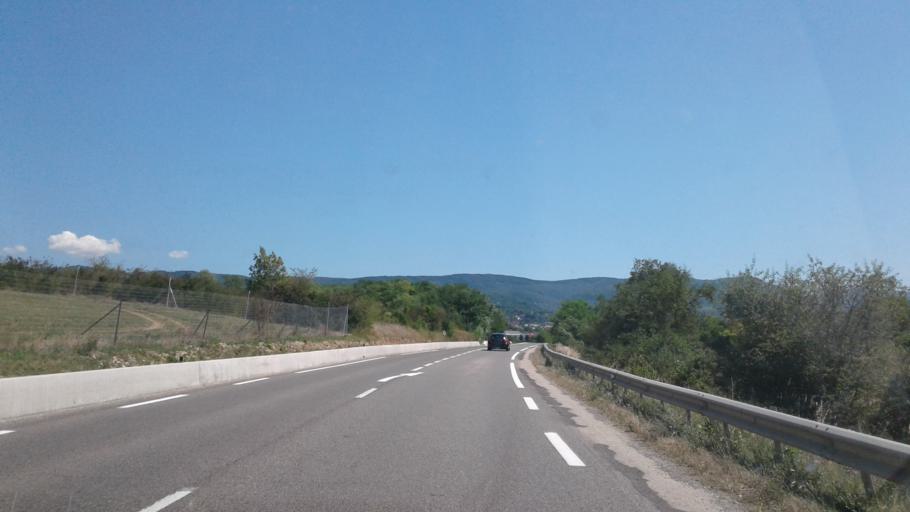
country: FR
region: Rhone-Alpes
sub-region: Departement de l'Ain
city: Chateau-Gaillard
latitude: 45.9766
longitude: 5.3263
